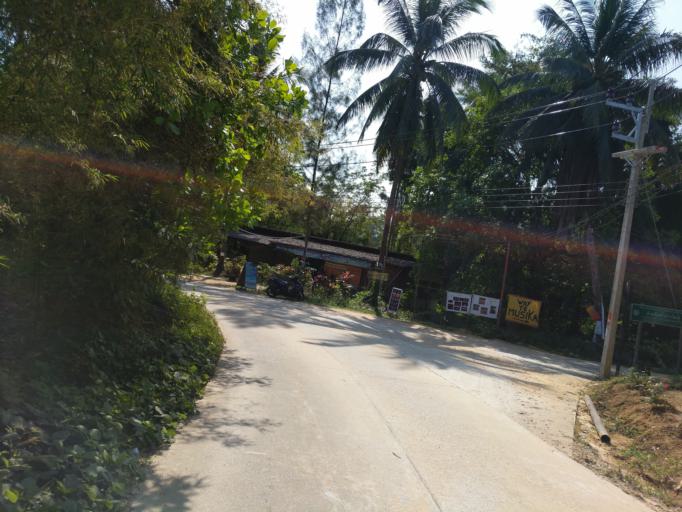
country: TH
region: Ranong
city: Kapoe
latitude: 9.7405
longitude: 98.4166
